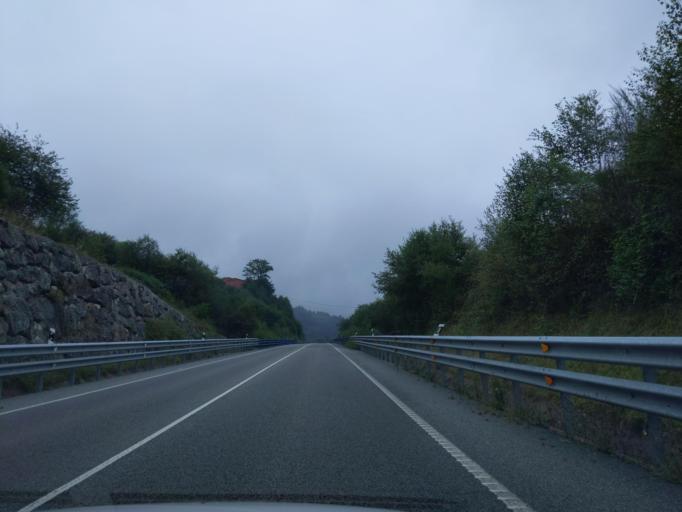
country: ES
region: Asturias
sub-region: Province of Asturias
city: Bimenes
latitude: 43.3351
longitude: -5.5844
